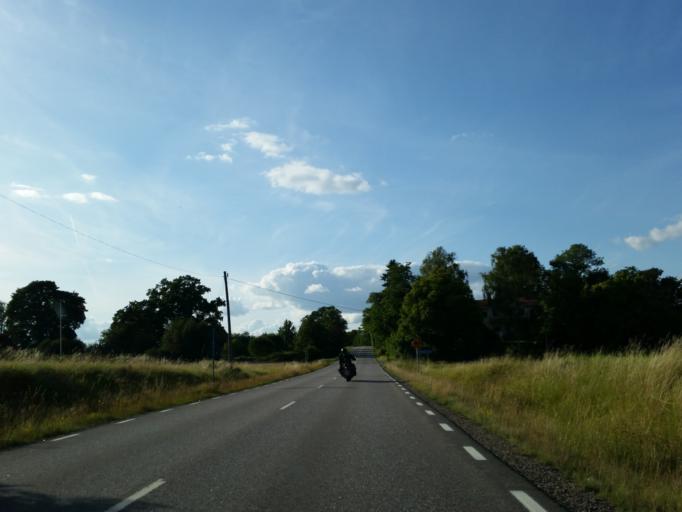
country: SE
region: Stockholm
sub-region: Sodertalje Kommun
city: Molnbo
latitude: 58.9970
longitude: 17.4086
